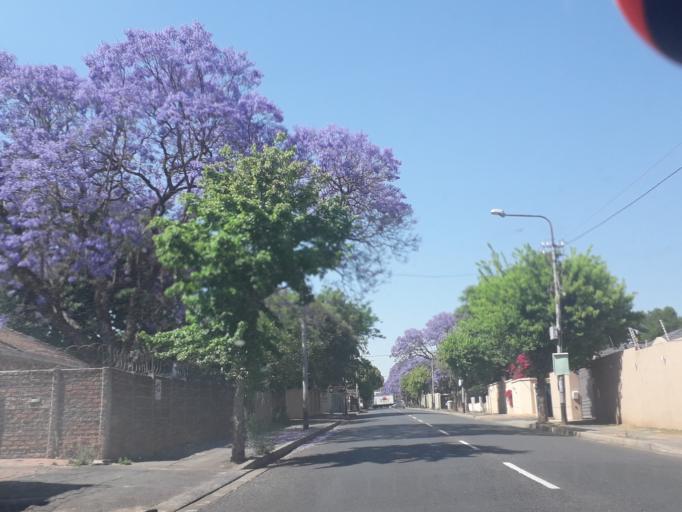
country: ZA
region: Gauteng
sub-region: City of Johannesburg Metropolitan Municipality
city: Johannesburg
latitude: -26.1542
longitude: 28.0768
